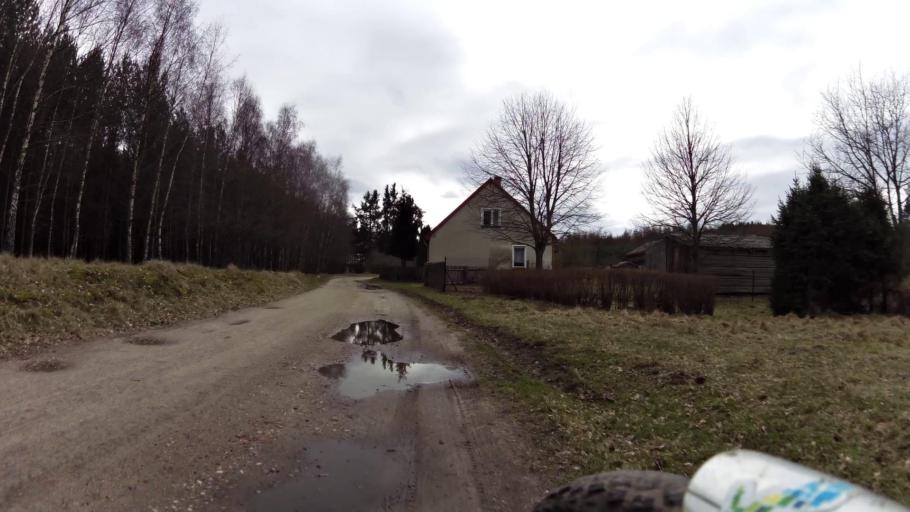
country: PL
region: Pomeranian Voivodeship
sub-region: Powiat bytowski
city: Kolczyglowy
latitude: 54.1552
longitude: 17.1870
